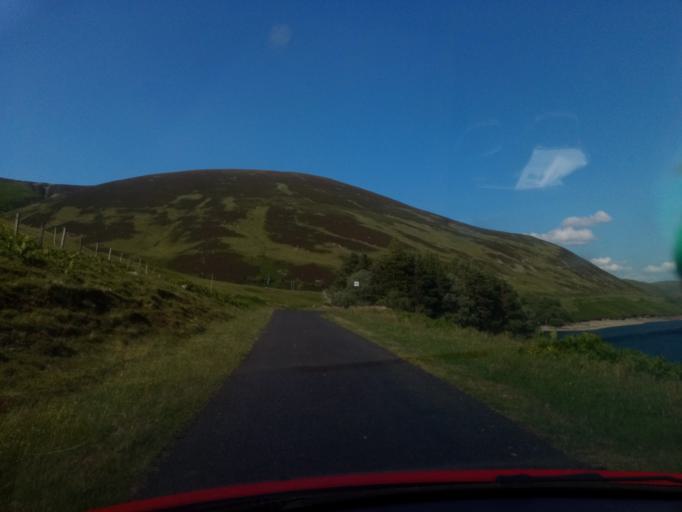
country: GB
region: Scotland
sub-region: Dumfries and Galloway
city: Moffat
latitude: 55.4831
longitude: -3.3024
